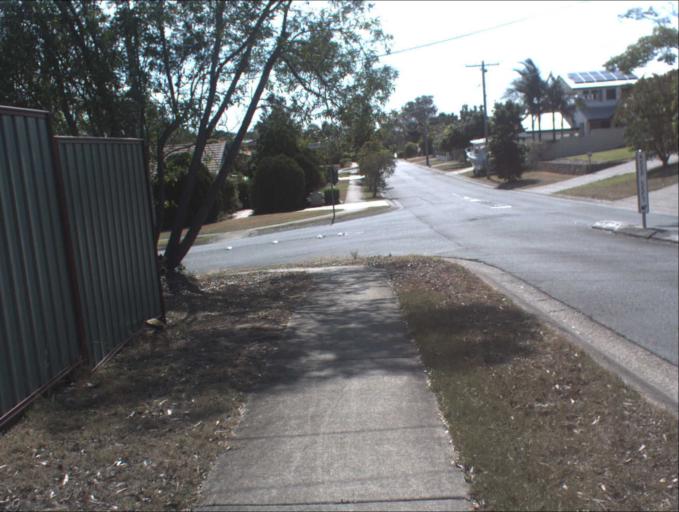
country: AU
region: Queensland
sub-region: Logan
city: Slacks Creek
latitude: -27.6578
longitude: 153.1787
